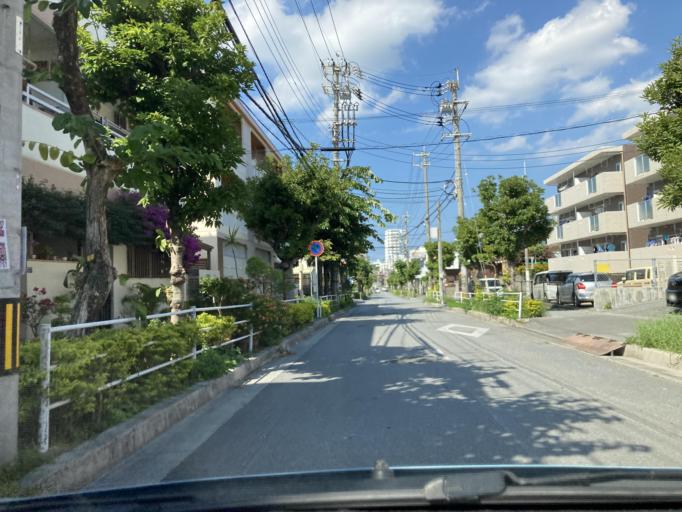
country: JP
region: Okinawa
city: Naha-shi
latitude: 26.2012
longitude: 127.6907
